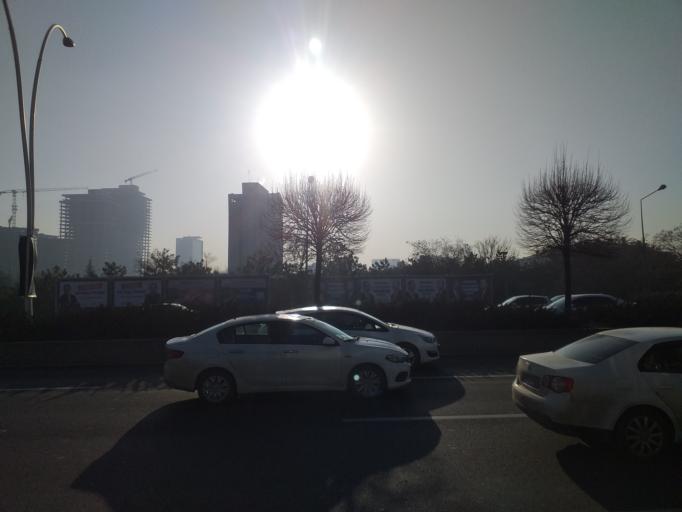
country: TR
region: Ankara
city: Ankara
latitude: 39.9421
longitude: 32.8274
